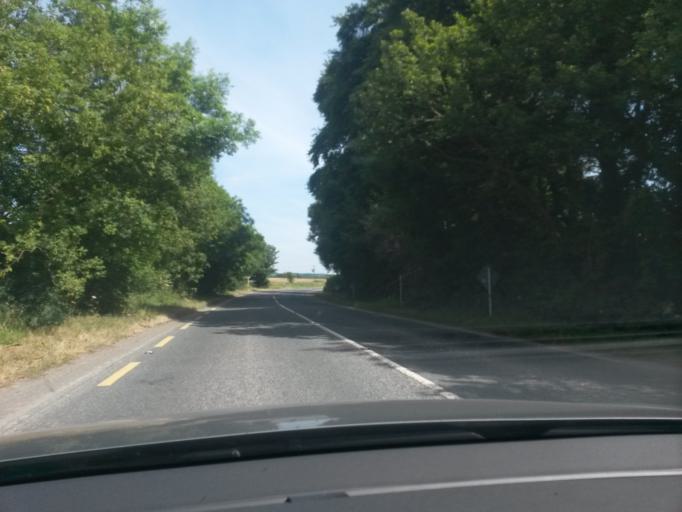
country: IE
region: Leinster
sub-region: Kildare
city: Naas
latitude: 53.2093
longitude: -6.6410
